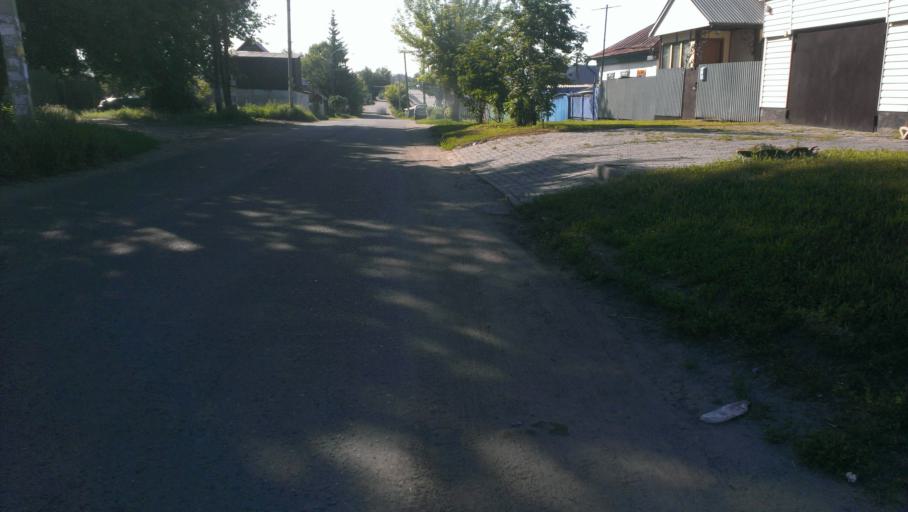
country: RU
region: Altai Krai
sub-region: Gorod Barnaulskiy
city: Barnaul
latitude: 53.3553
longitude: 83.7507
